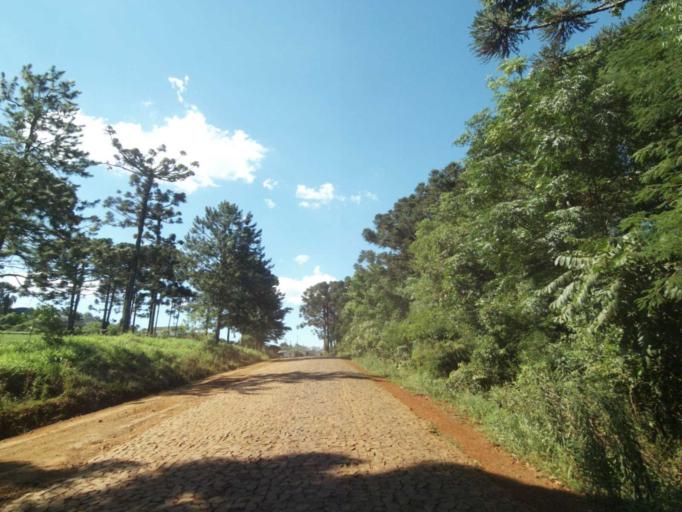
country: BR
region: Parana
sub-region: Laranjeiras Do Sul
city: Laranjeiras do Sul
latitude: -25.3863
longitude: -52.2020
